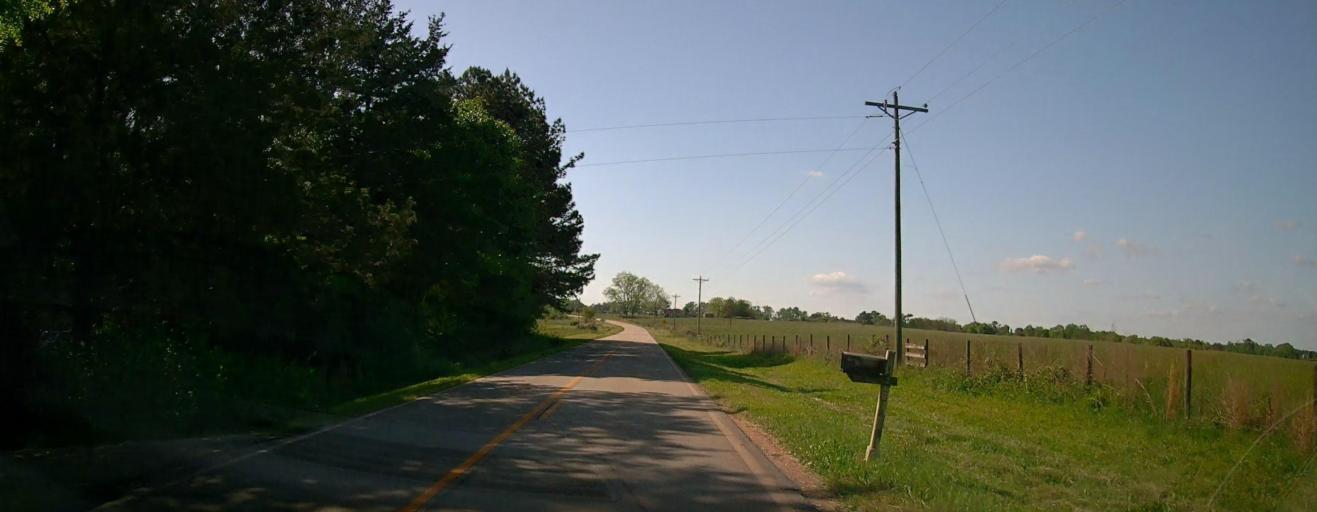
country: US
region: Georgia
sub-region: Morgan County
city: Madison
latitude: 33.6599
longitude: -83.4771
